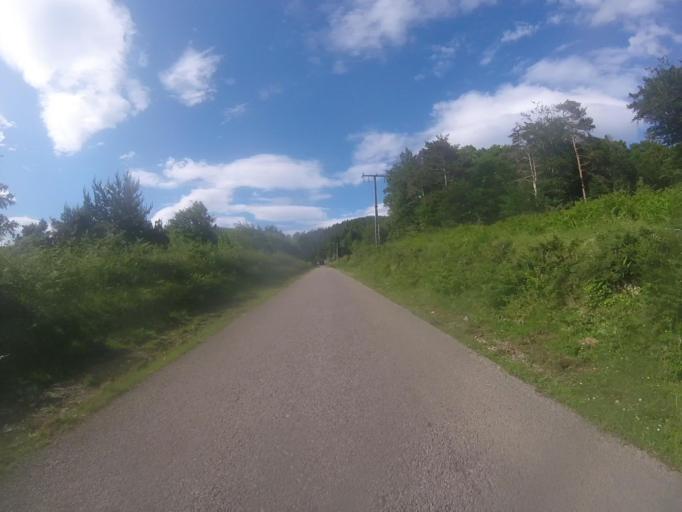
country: ES
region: Navarre
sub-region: Provincia de Navarra
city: Arantza
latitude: 43.2377
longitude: -1.8038
